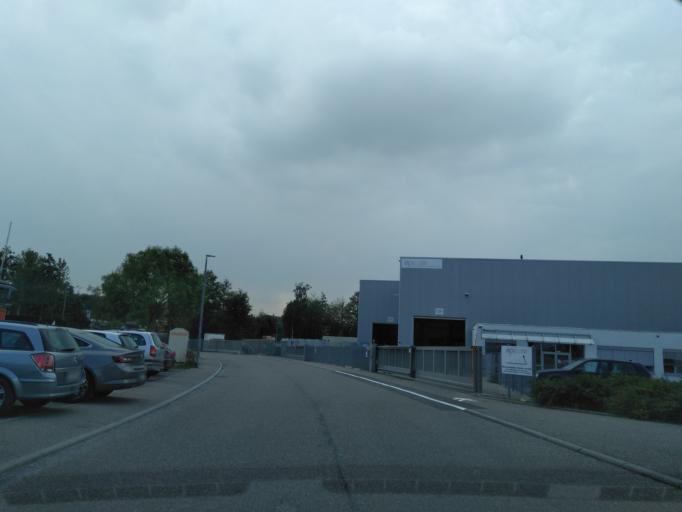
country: DE
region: Baden-Wuerttemberg
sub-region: Regierungsbezirk Stuttgart
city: Sersheim
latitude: 48.9580
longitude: 9.0039
